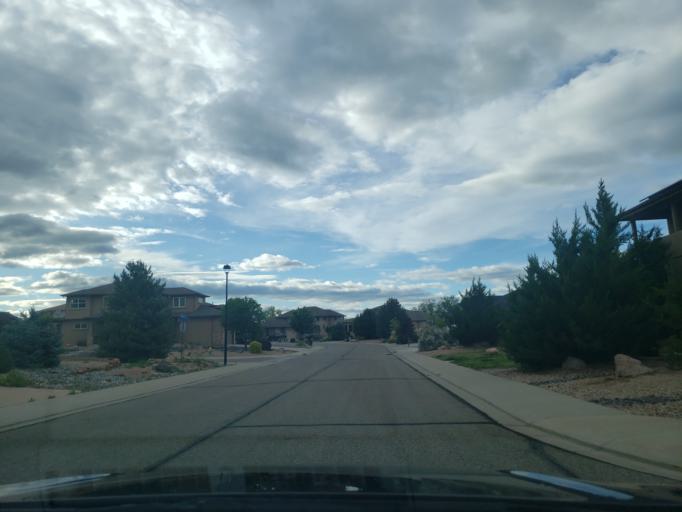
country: US
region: Colorado
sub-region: Mesa County
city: Redlands
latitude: 39.1053
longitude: -108.6648
